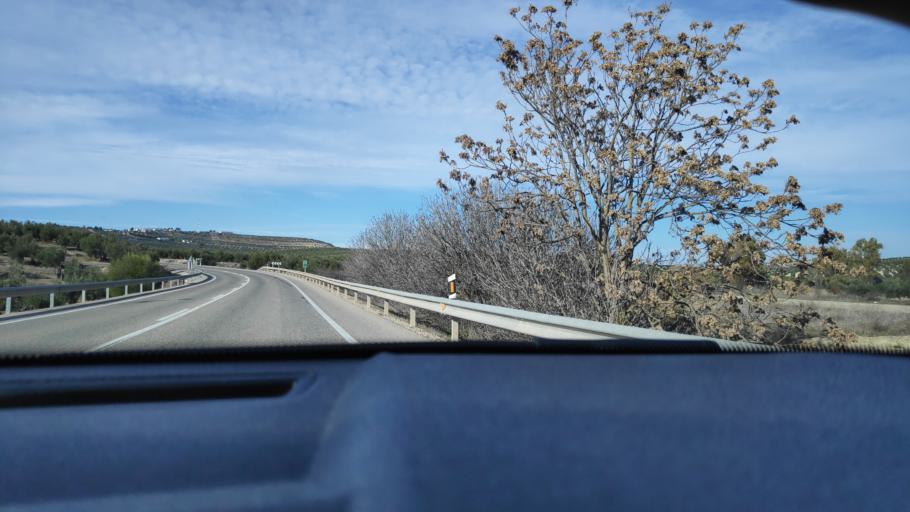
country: ES
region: Andalusia
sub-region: Provincia de Jaen
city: Porcuna
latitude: 37.8596
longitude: -4.1468
